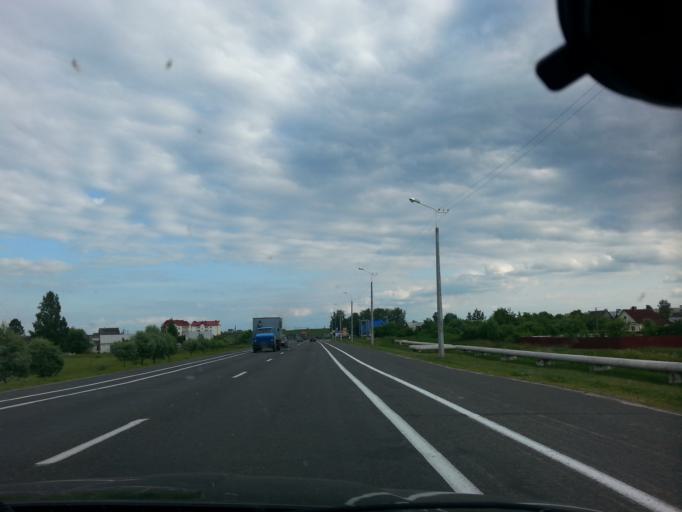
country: BY
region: Minsk
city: Myadzyel
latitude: 54.8789
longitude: 26.9402
